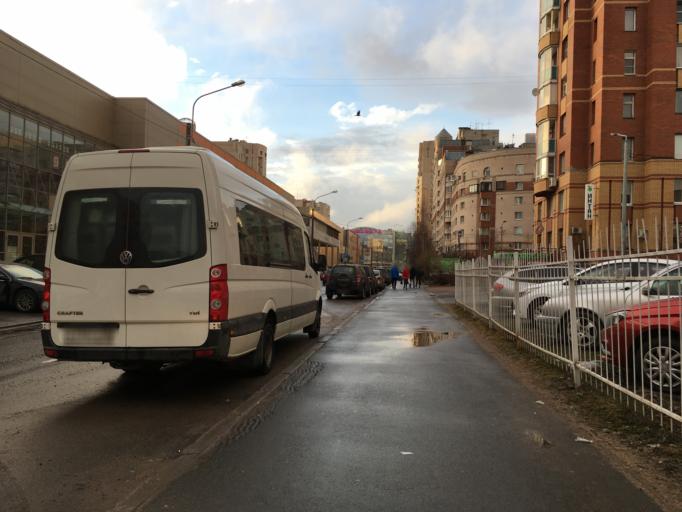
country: RU
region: St.-Petersburg
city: Komendantsky aerodrom
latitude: 60.0042
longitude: 30.2646
